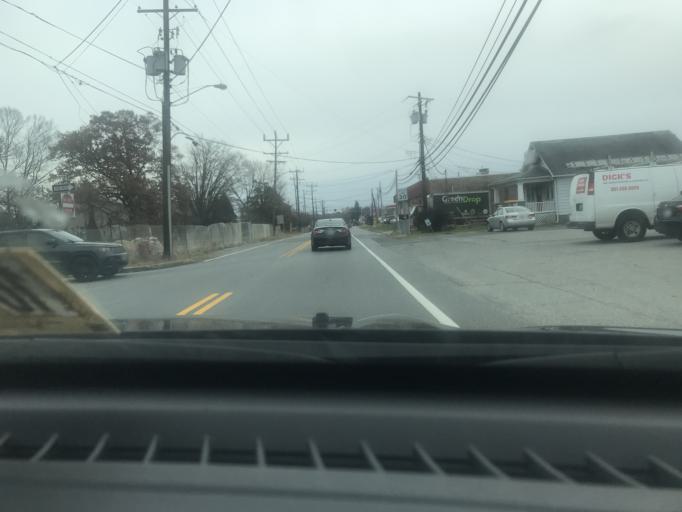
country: US
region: Maryland
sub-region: Prince George's County
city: Camp Springs
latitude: 38.8054
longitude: -76.9085
